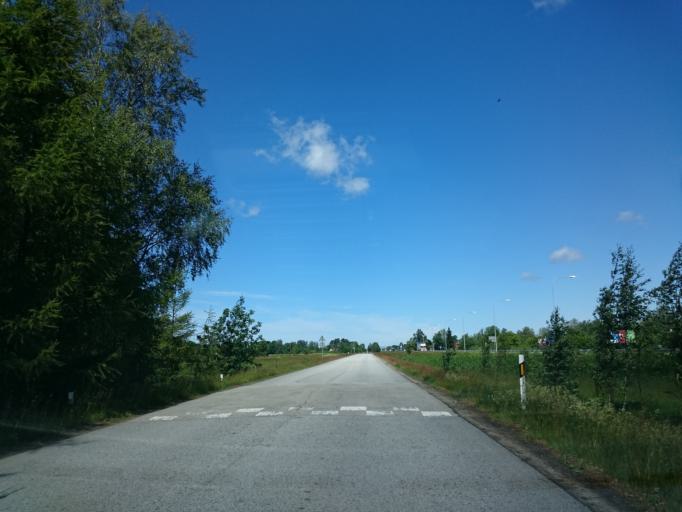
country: LV
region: Adazi
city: Adazi
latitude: 57.0717
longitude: 24.3185
